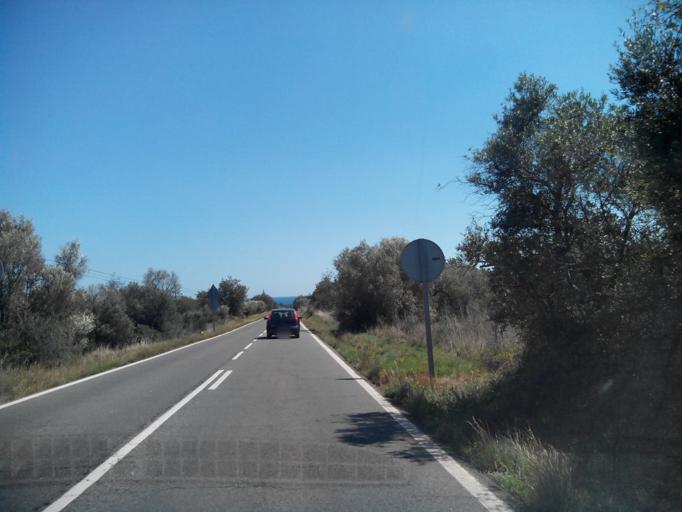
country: ES
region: Catalonia
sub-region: Provincia de Tarragona
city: Vilanova d'Escornalbou
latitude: 41.0755
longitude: 0.9711
